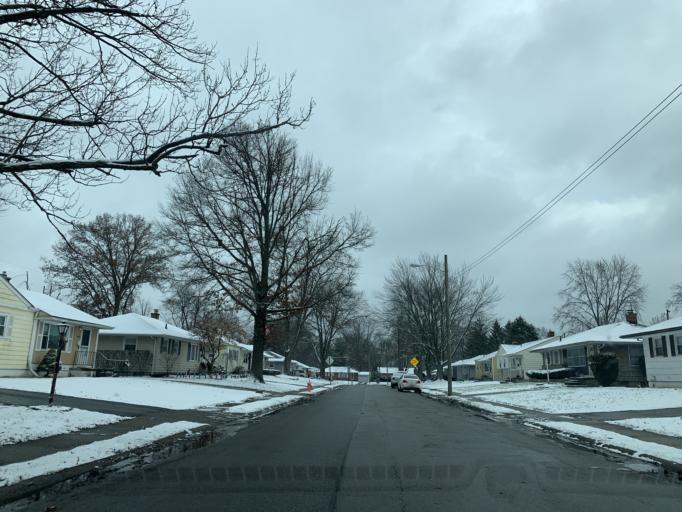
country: US
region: Ohio
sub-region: Franklin County
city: Minerva Park
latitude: 40.0540
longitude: -82.9645
